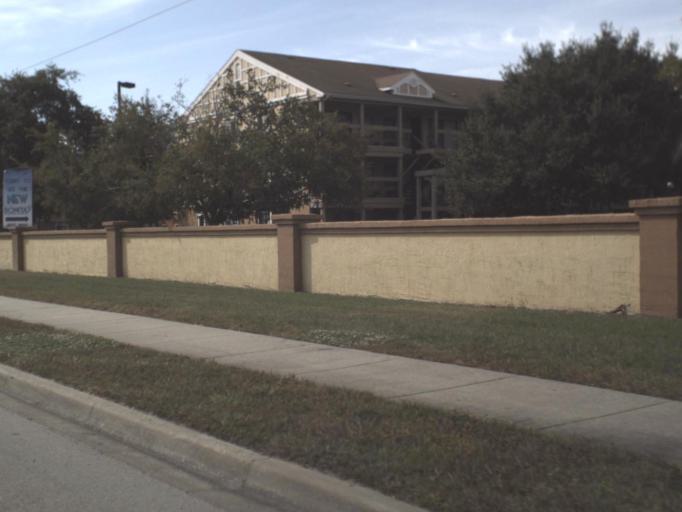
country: US
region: Florida
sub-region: Orange County
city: Oak Ridge
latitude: 28.4793
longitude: -81.4177
